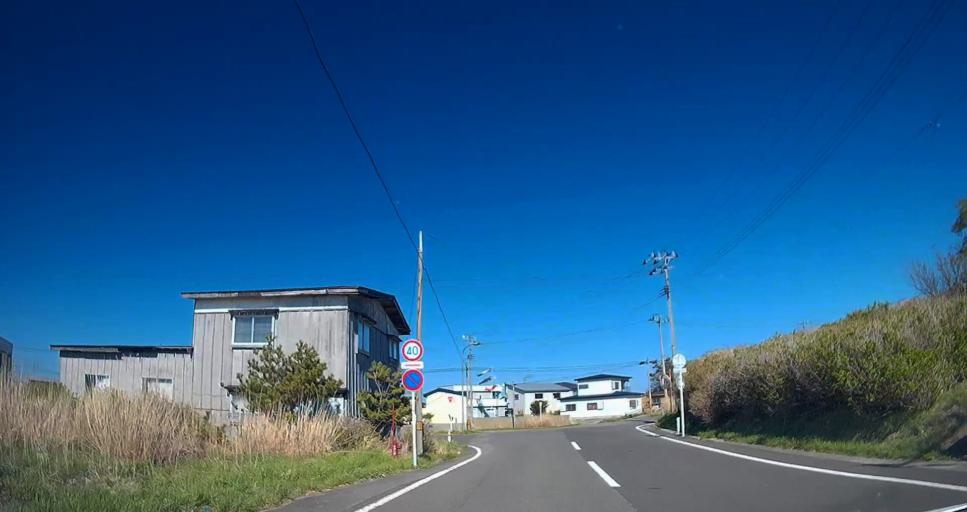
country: JP
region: Hokkaido
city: Hakodate
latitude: 41.5439
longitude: 140.9137
